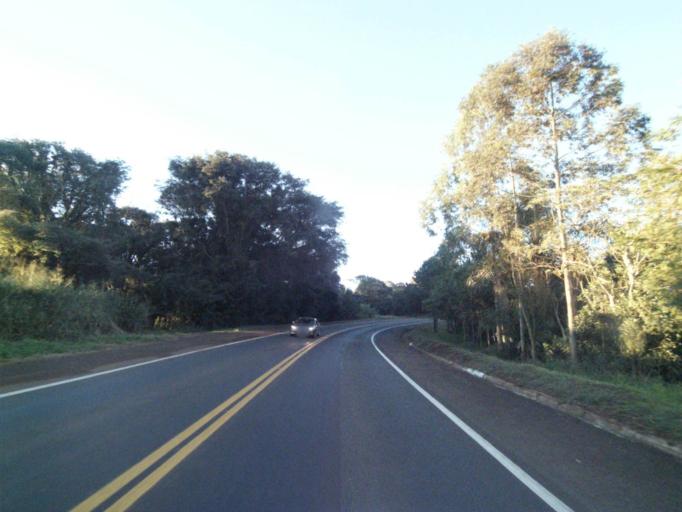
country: BR
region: Parana
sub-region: Faxinal
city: Faxinal
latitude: -23.7528
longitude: -51.1359
